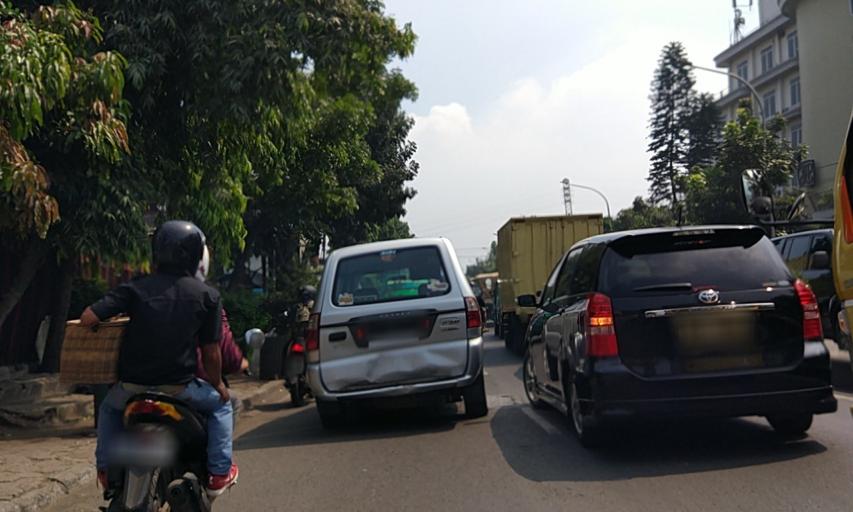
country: ID
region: West Java
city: Cimahi
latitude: -6.9091
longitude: 107.5681
